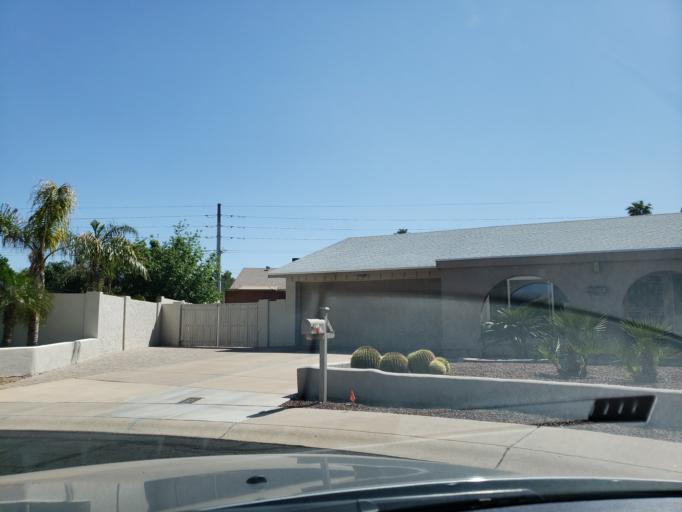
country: US
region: Arizona
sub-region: Maricopa County
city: Paradise Valley
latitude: 33.5830
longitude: -112.0317
